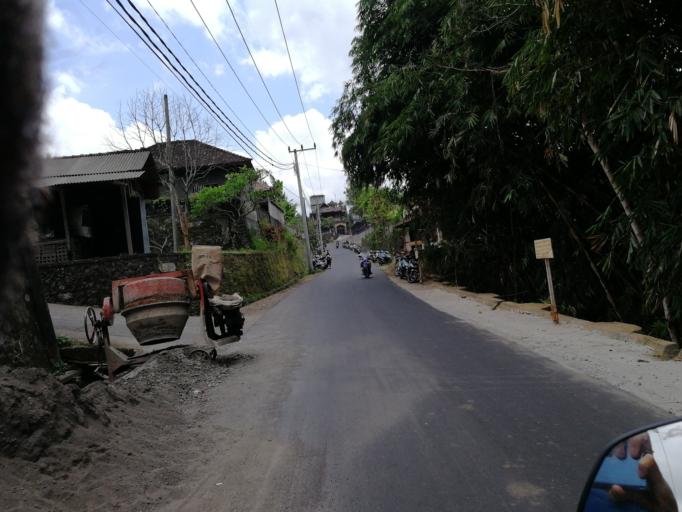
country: ID
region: Bali
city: Banjar Wangsian
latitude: -8.4662
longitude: 115.4468
